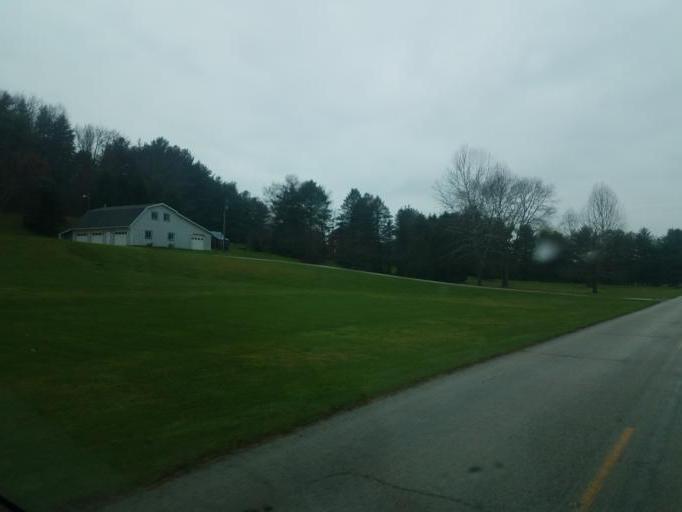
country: US
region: Ohio
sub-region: Sandusky County
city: Bellville
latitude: 40.6225
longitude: -82.5439
